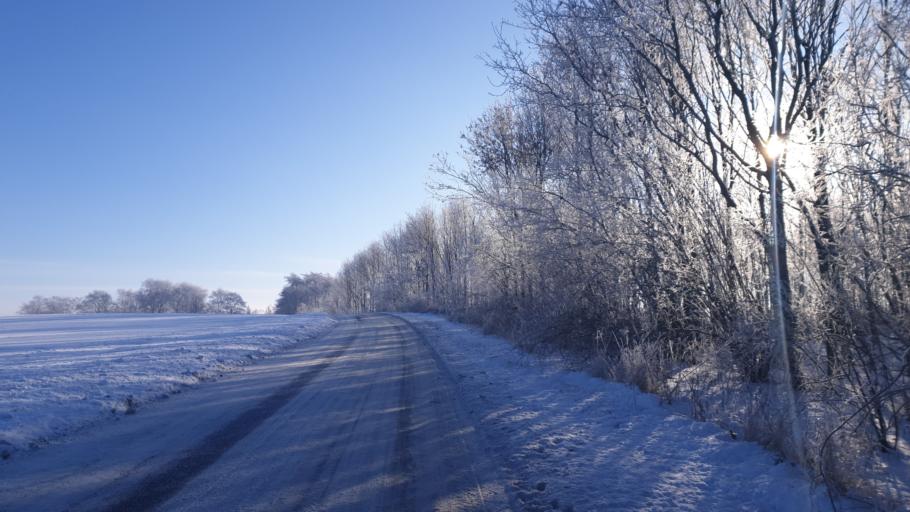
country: DK
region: Central Jutland
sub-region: Hedensted Kommune
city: Hedensted
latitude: 55.8064
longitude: 9.7280
